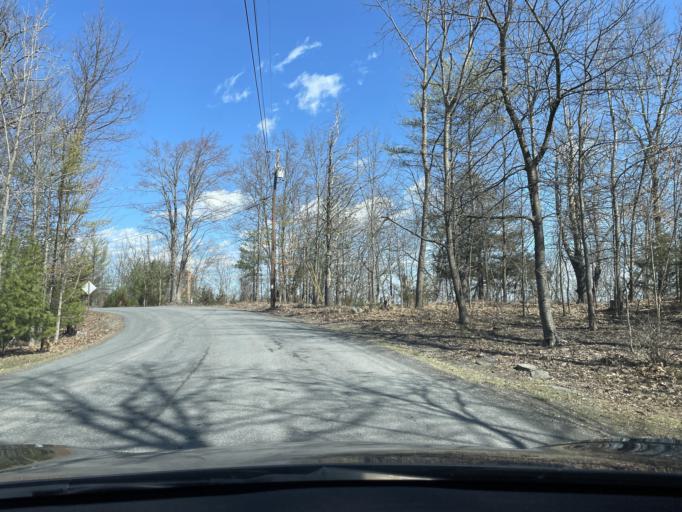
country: US
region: New York
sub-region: Ulster County
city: West Hurley
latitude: 41.9702
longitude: -74.1050
